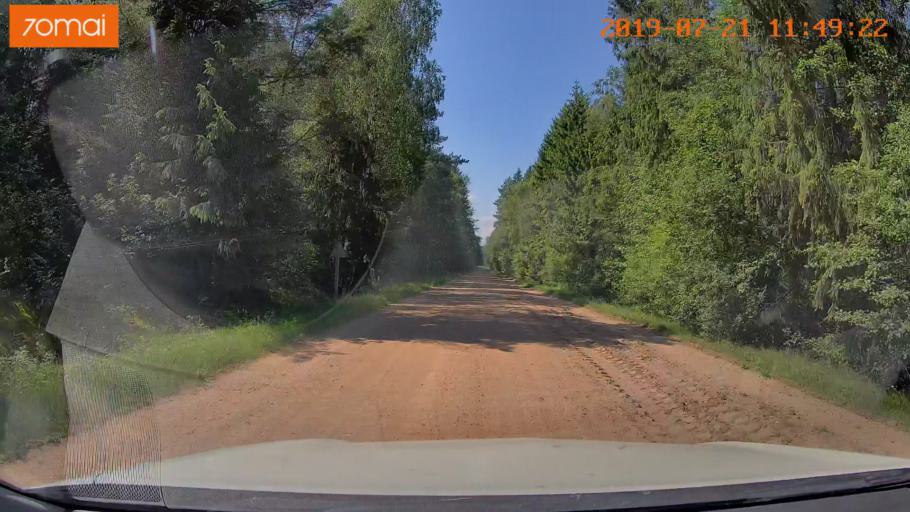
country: BY
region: Grodnenskaya
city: Lyubcha
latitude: 53.8928
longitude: 26.0397
